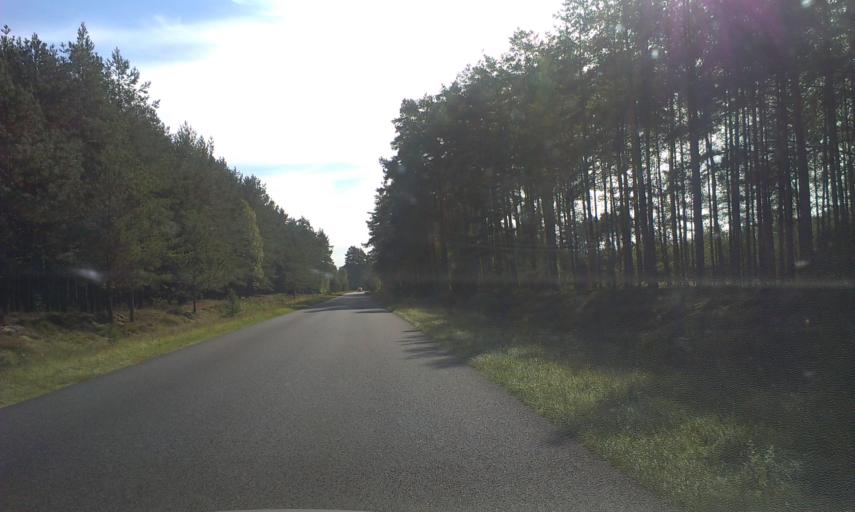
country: PL
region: Greater Poland Voivodeship
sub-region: Powiat zlotowski
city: Okonek
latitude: 53.5175
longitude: 16.9713
